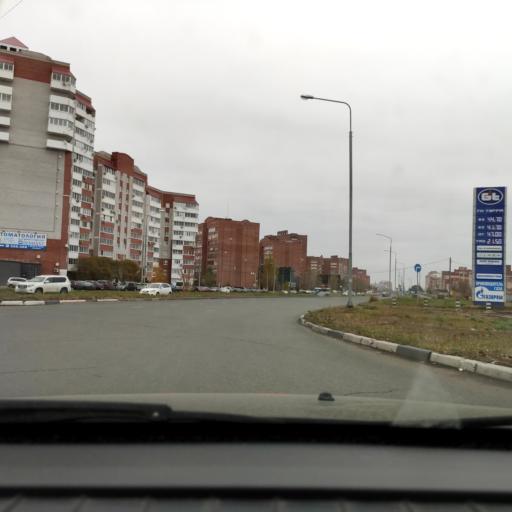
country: RU
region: Samara
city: Tol'yatti
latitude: 53.5323
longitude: 49.3441
